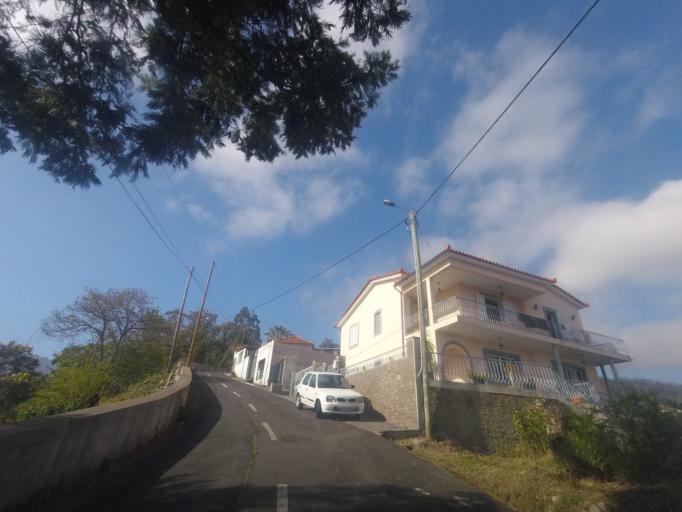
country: PT
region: Madeira
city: Camara de Lobos
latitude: 32.6770
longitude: -16.9539
